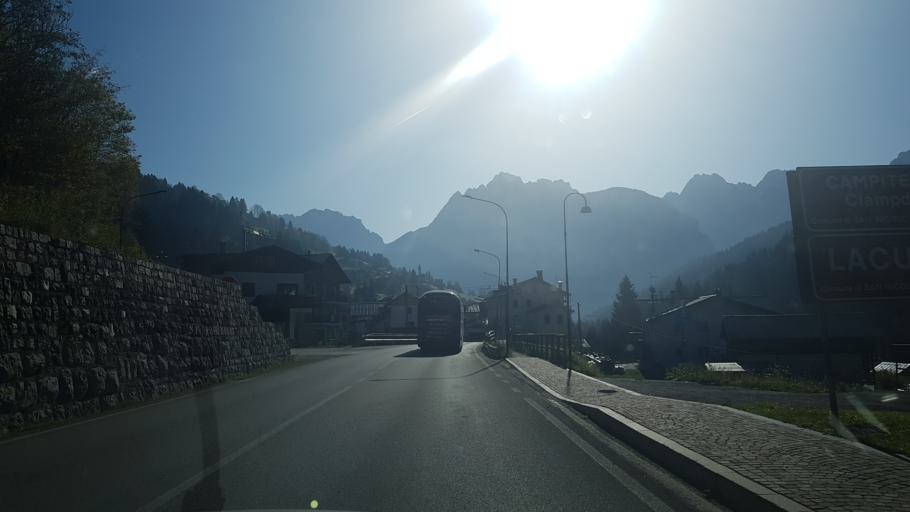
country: IT
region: Veneto
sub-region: Provincia di Belluno
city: San Nicolo Comelico
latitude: 46.5786
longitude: 12.5294
